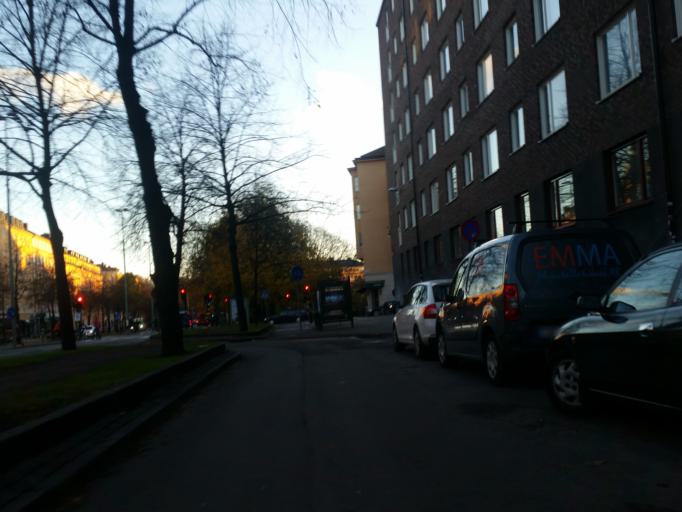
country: SE
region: Stockholm
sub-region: Stockholms Kommun
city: Stockholm
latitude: 59.3085
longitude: 18.0818
